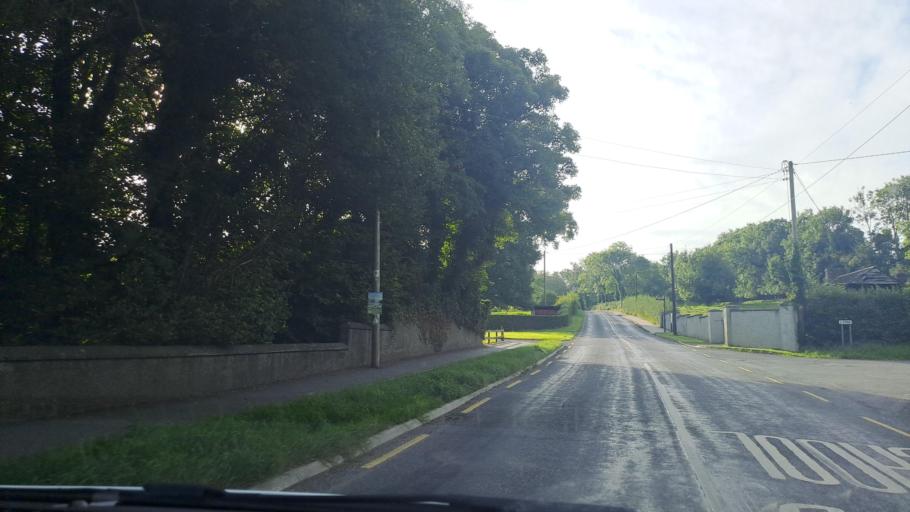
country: IE
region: Ulster
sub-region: An Cabhan
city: Kingscourt
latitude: 53.9191
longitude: -6.8112
